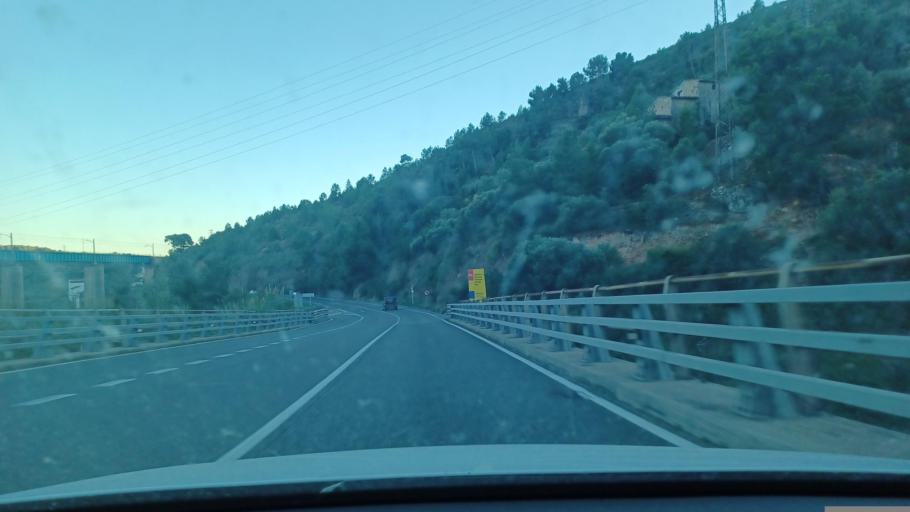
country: ES
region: Catalonia
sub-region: Provincia de Tarragona
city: Alcover
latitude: 41.3065
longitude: 1.1923
